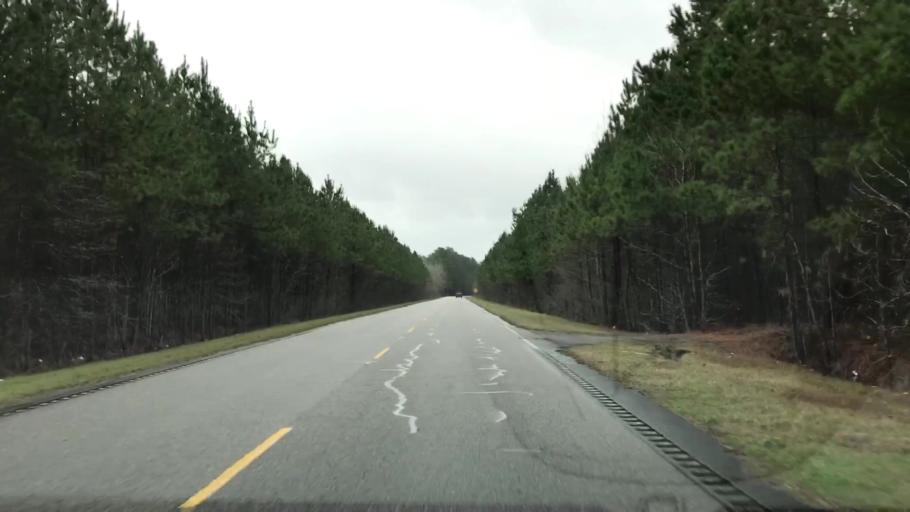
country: US
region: South Carolina
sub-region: Williamsburg County
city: Andrews
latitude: 33.5652
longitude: -79.4533
